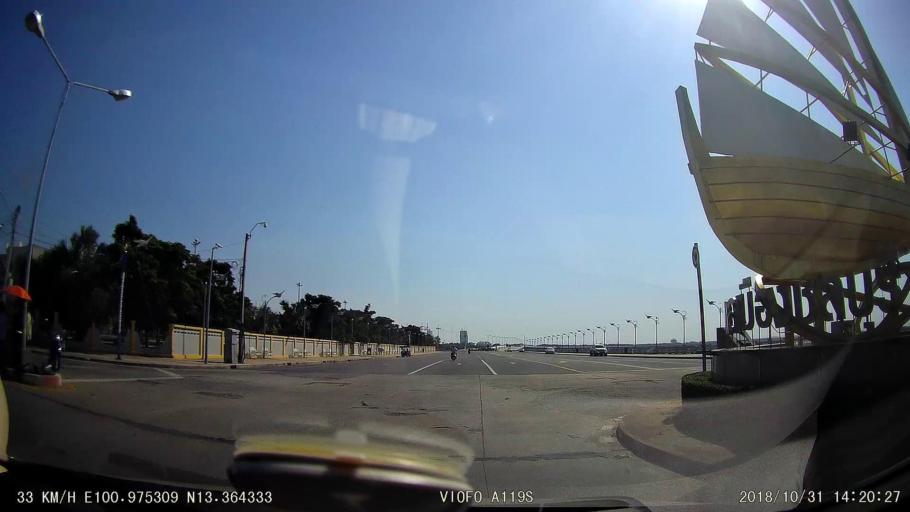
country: TH
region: Chon Buri
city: Chon Buri
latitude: 13.3642
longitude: 100.9753
